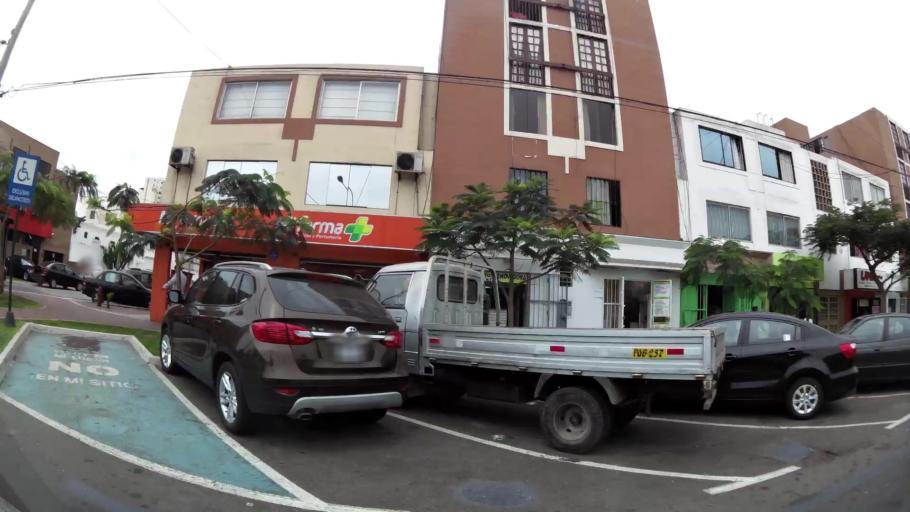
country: PE
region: Lima
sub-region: Lima
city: San Isidro
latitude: -12.0897
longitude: -77.0479
